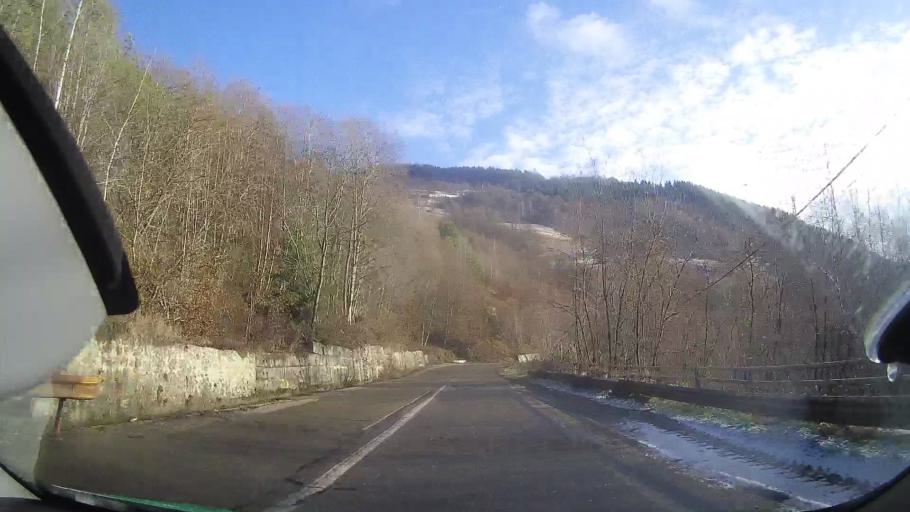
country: RO
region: Alba
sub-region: Comuna Sohodol
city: Sohodol
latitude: 46.3798
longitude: 23.0114
